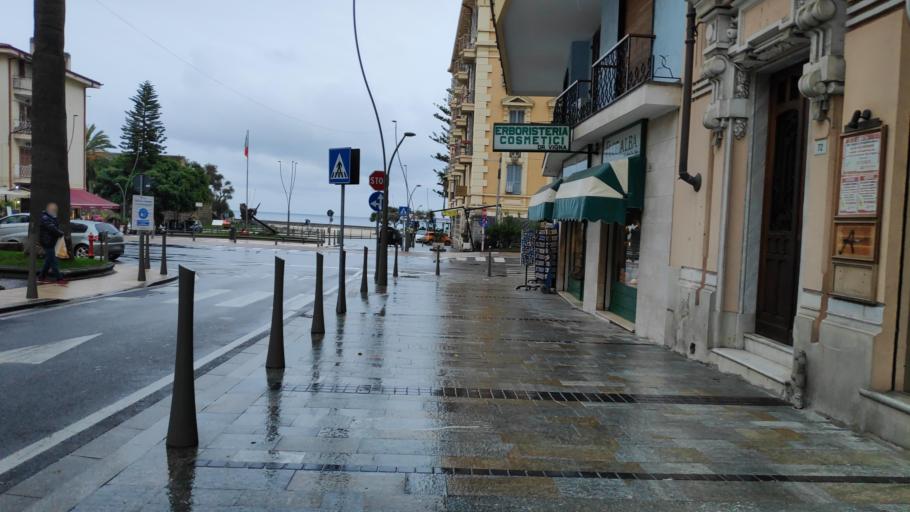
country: IT
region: Liguria
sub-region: Provincia di Imperia
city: San Remo
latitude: 43.8151
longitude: 7.7765
